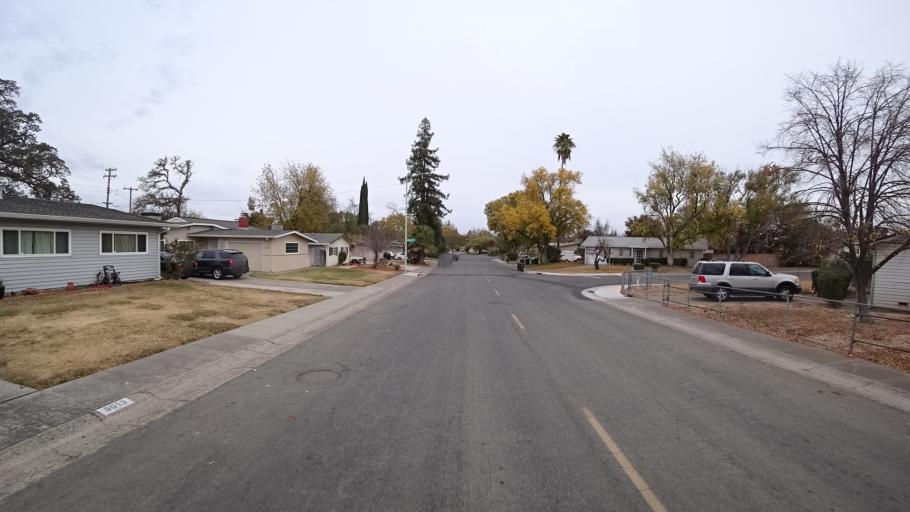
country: US
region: California
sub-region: Sacramento County
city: Citrus Heights
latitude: 38.7117
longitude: -121.2963
